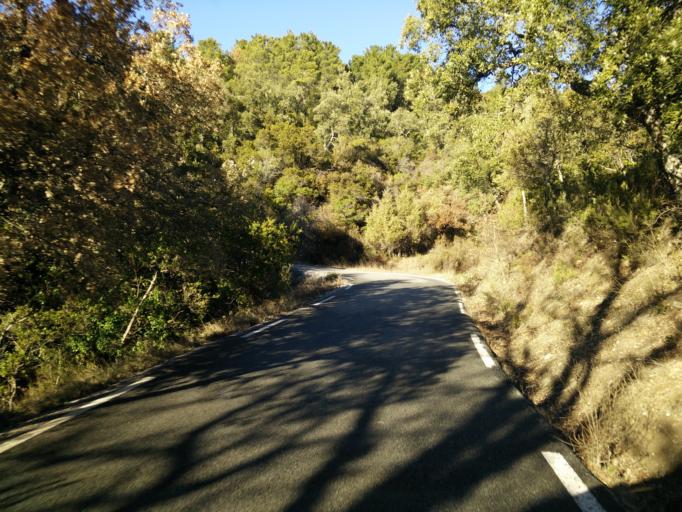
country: FR
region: Provence-Alpes-Cote d'Azur
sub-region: Departement du Var
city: Collobrieres
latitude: 43.2372
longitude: 6.3595
